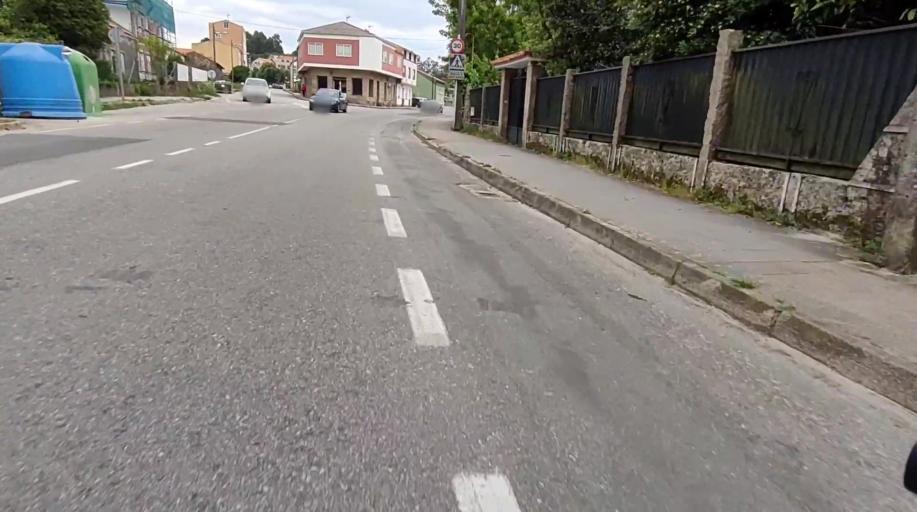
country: ES
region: Galicia
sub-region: Provincia da Coruna
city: Boiro
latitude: 42.6366
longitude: -8.8759
